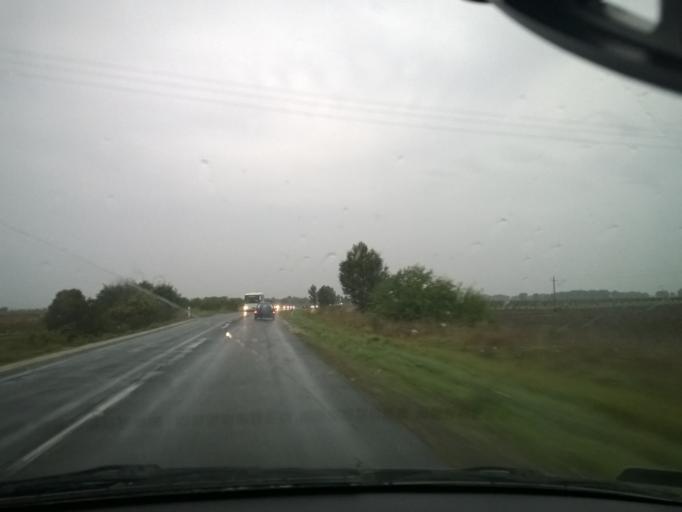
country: HU
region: Pest
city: Kiskunlachaza
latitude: 47.1432
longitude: 18.9955
